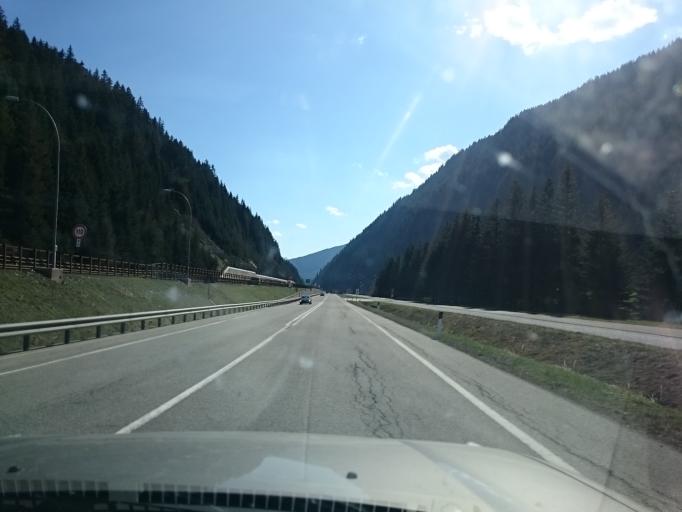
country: IT
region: Trentino-Alto Adige
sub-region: Bolzano
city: Colle Isarco
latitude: 46.9713
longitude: 11.4733
